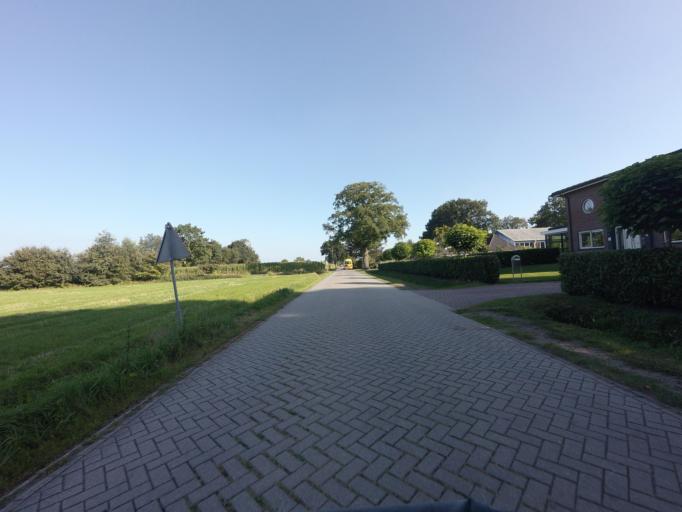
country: NL
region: Overijssel
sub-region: Gemeente Hardenberg
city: Hardenberg
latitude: 52.5620
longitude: 6.6360
